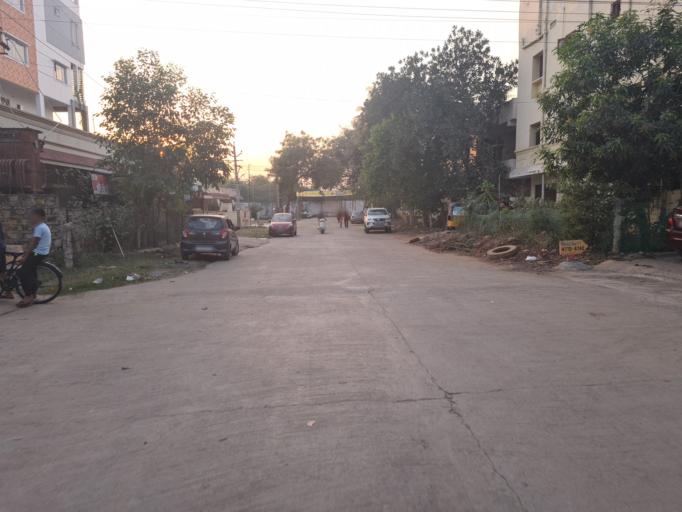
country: IN
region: Telangana
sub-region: Medak
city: Serilingampalle
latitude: 17.4778
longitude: 78.2831
